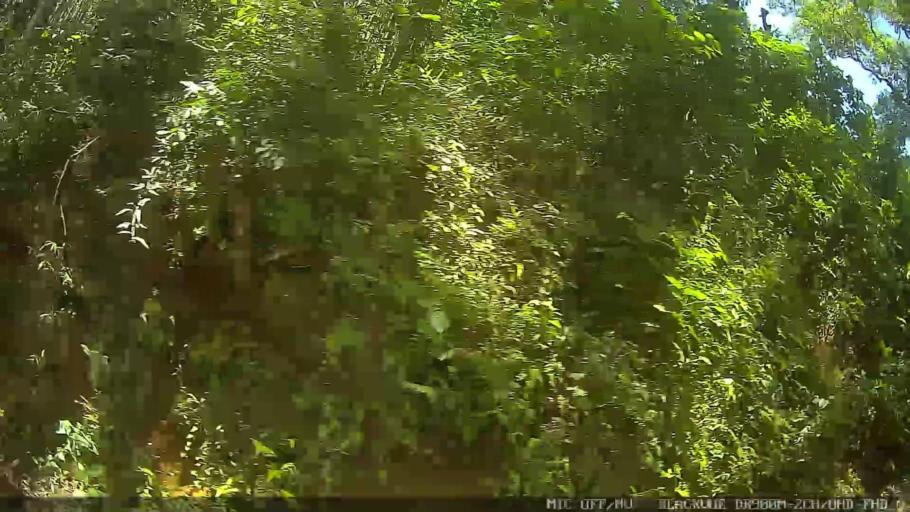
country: BR
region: Minas Gerais
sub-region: Extrema
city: Extrema
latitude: -22.8876
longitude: -46.2949
